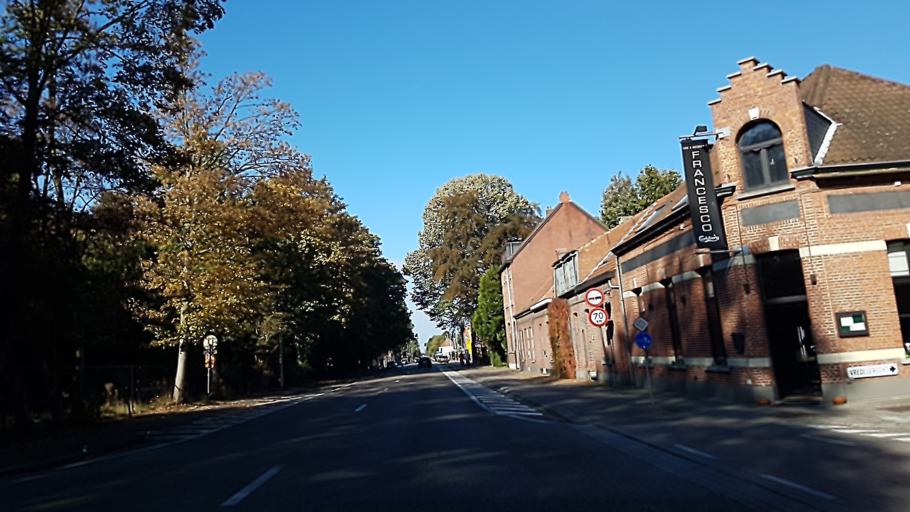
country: BE
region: Flanders
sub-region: Provincie Antwerpen
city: Kapellen
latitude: 51.3261
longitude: 4.4186
